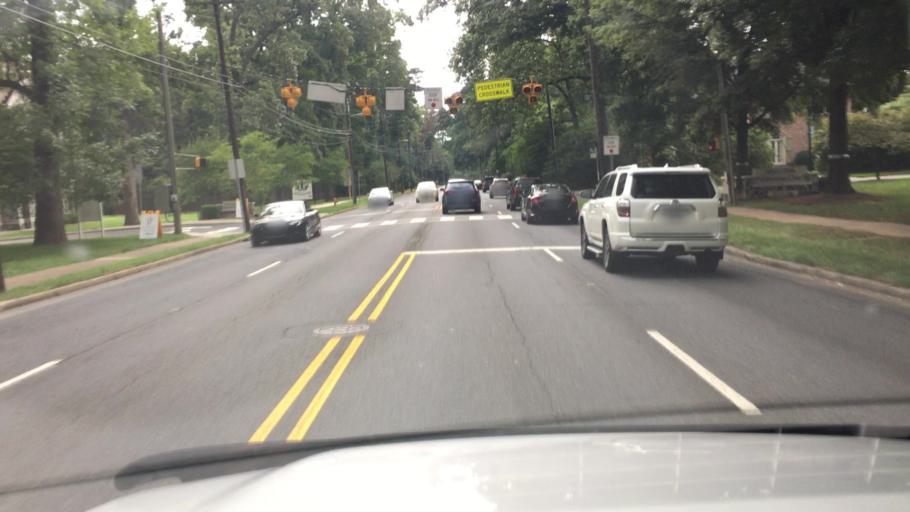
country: US
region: North Carolina
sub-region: Mecklenburg County
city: Charlotte
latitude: 35.1939
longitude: -80.8256
